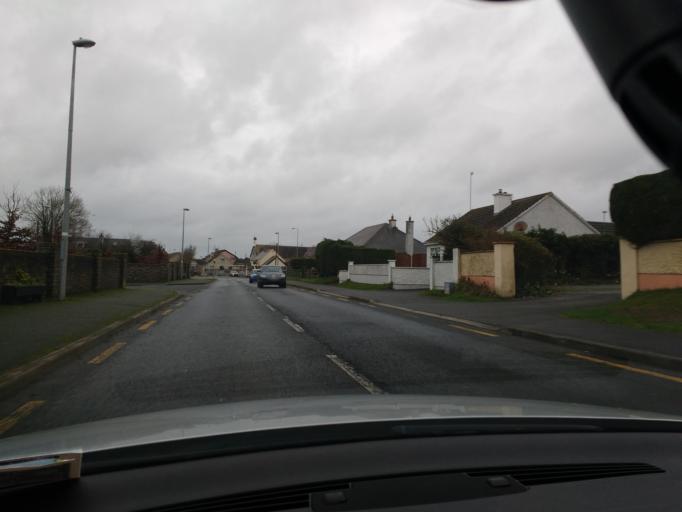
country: IE
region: Munster
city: Thurles
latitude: 52.6723
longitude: -7.7092
